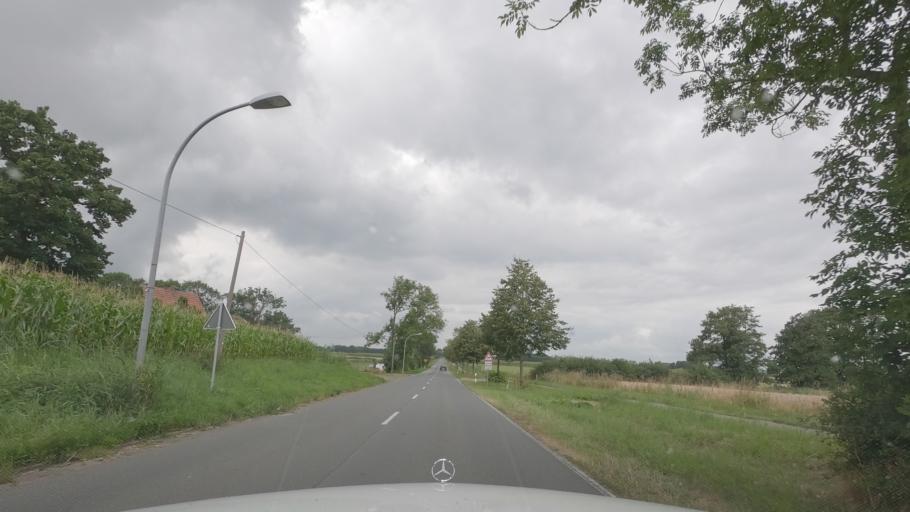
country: DE
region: Lower Saxony
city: Neuenkirchen
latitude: 53.2392
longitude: 8.5274
